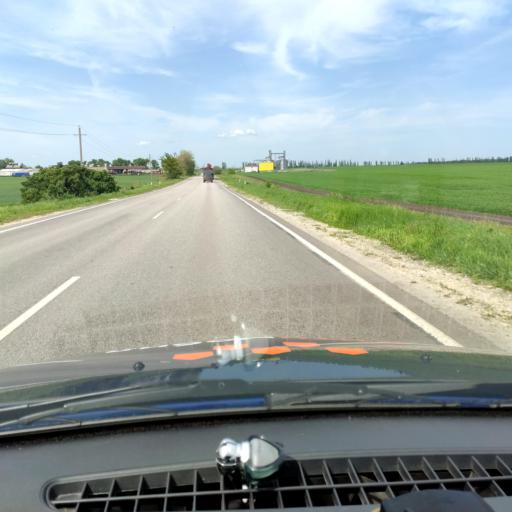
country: RU
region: Voronezj
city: Novaya Usman'
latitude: 51.5751
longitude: 39.3752
